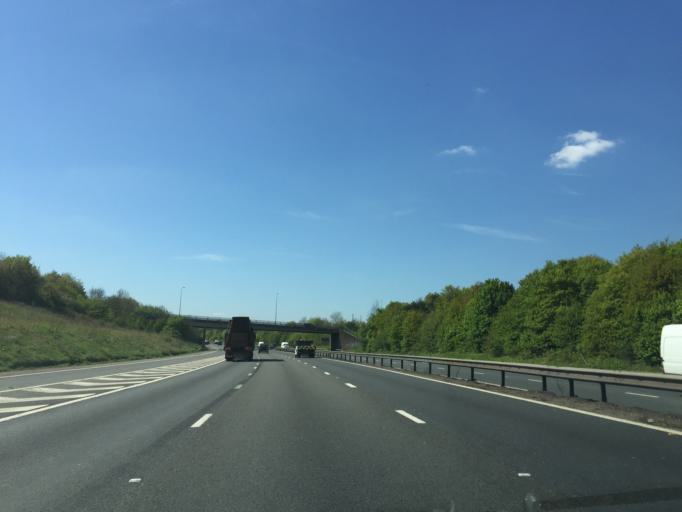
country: GB
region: England
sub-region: Essex
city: Chigwell
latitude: 51.6275
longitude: 0.0667
